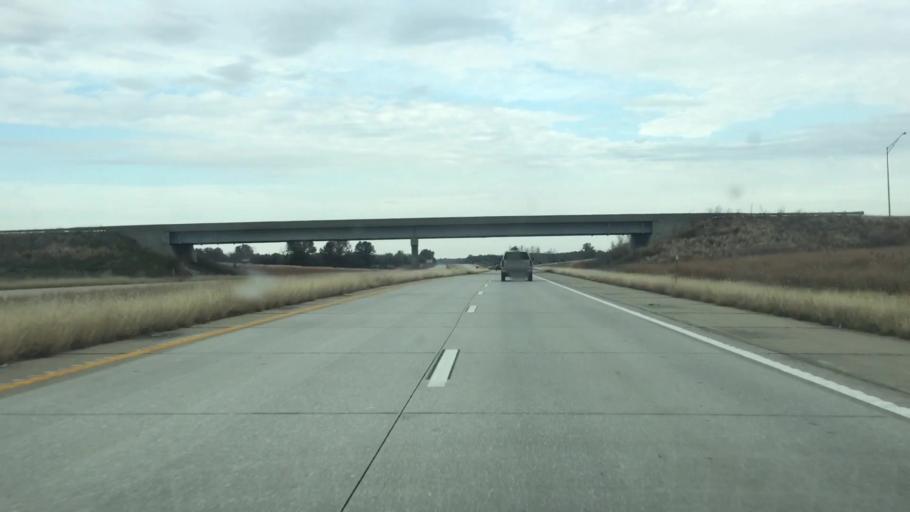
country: US
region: Missouri
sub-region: Henry County
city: Clinton
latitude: 38.2489
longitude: -93.7617
